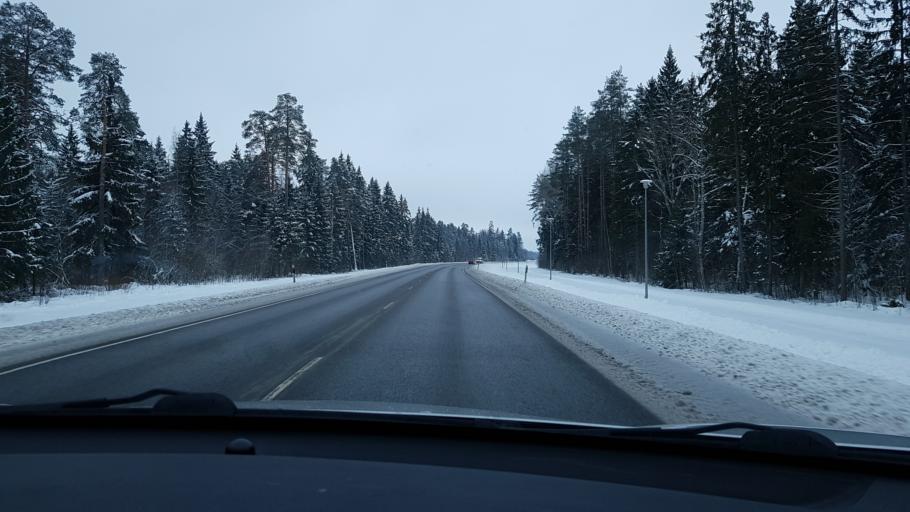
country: EE
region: Jaervamaa
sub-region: Paide linn
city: Paide
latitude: 58.8646
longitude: 25.4922
